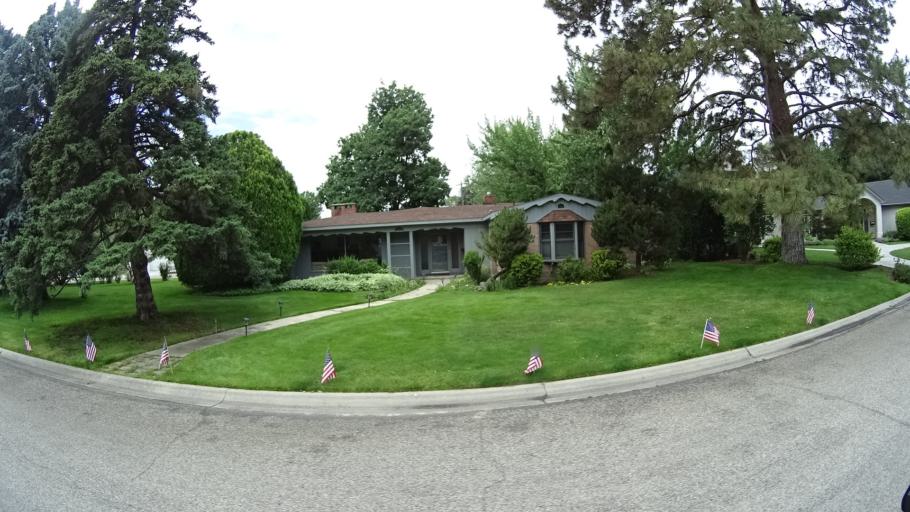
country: US
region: Idaho
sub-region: Ada County
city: Boise
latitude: 43.6078
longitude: -116.2218
